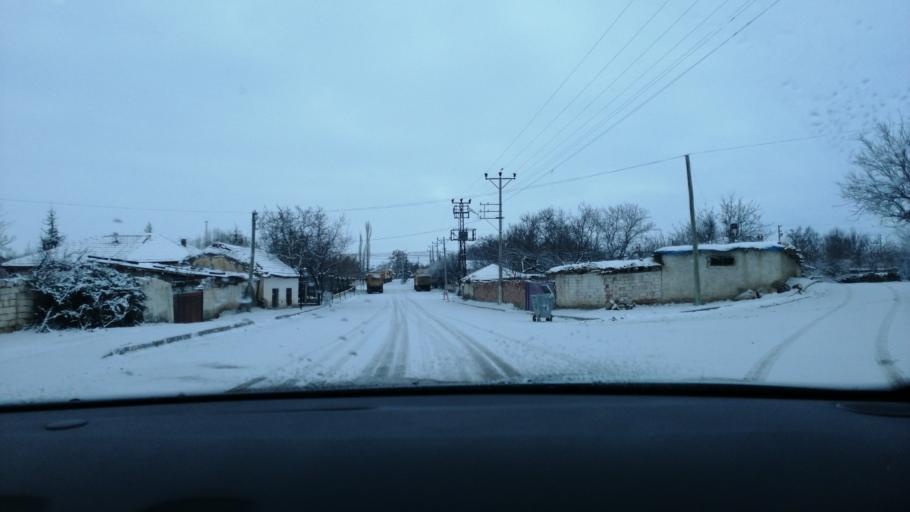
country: TR
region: Aksaray
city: Agacoren
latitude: 38.9323
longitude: 33.9489
